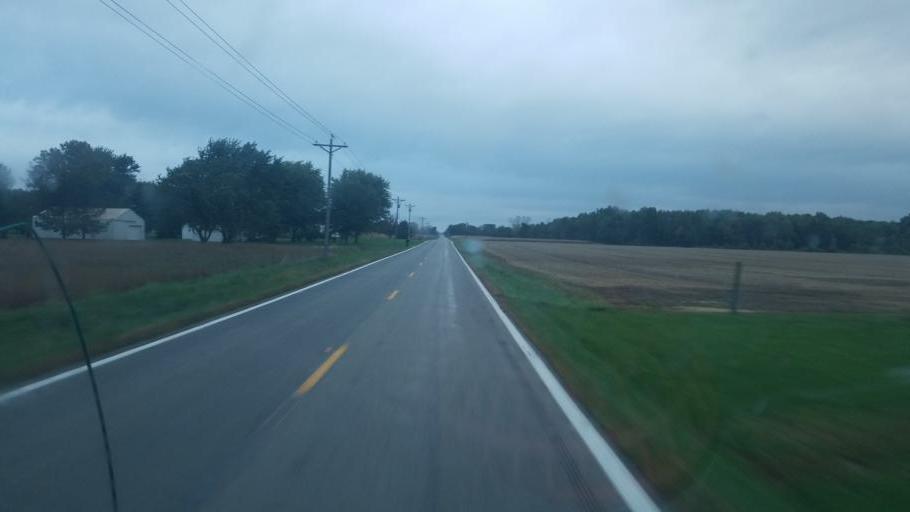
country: US
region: Ohio
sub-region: Morrow County
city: Cardington
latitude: 40.5685
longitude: -82.9622
